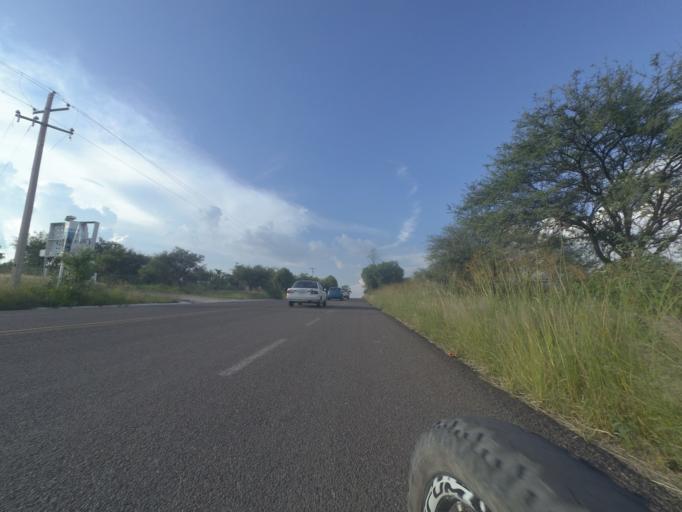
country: MX
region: Aguascalientes
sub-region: Aguascalientes
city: Penuelas (El Cienegal)
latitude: 21.7456
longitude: -102.3511
